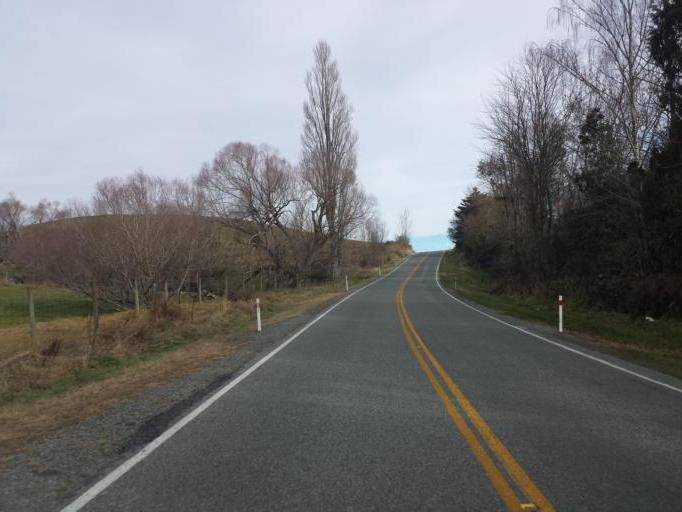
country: NZ
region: Canterbury
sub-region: Timaru District
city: Pleasant Point
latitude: -44.1181
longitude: 171.1305
